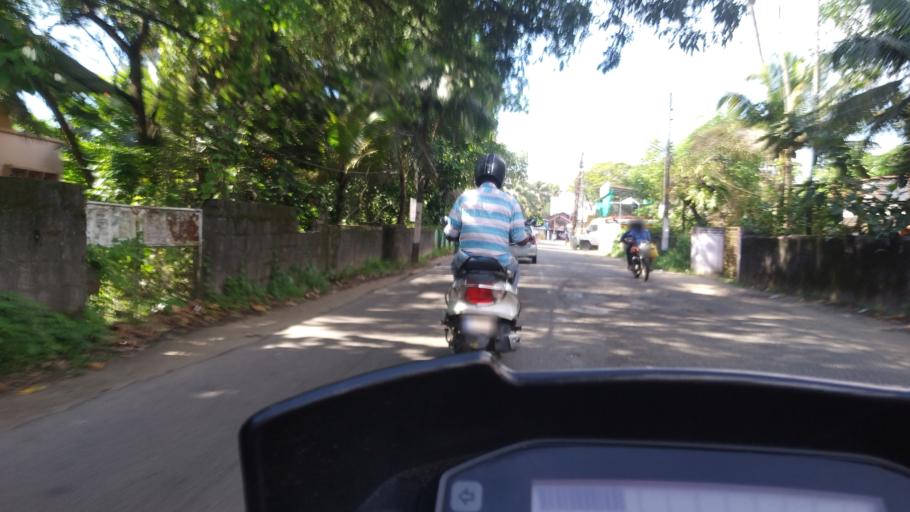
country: IN
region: Kerala
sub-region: Ernakulam
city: Elur
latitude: 10.0585
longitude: 76.2144
